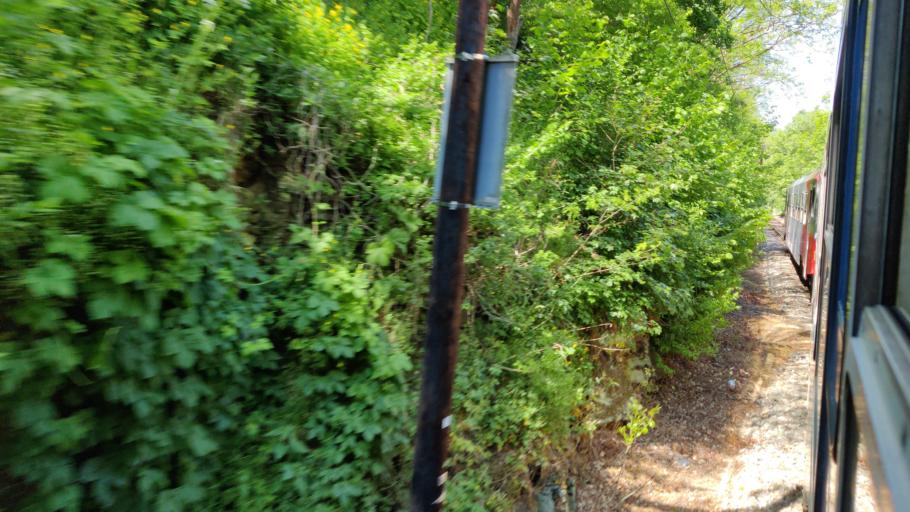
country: AT
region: Lower Austria
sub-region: Politischer Bezirk Horn
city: Gars am Kamp
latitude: 48.6109
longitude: 15.6559
